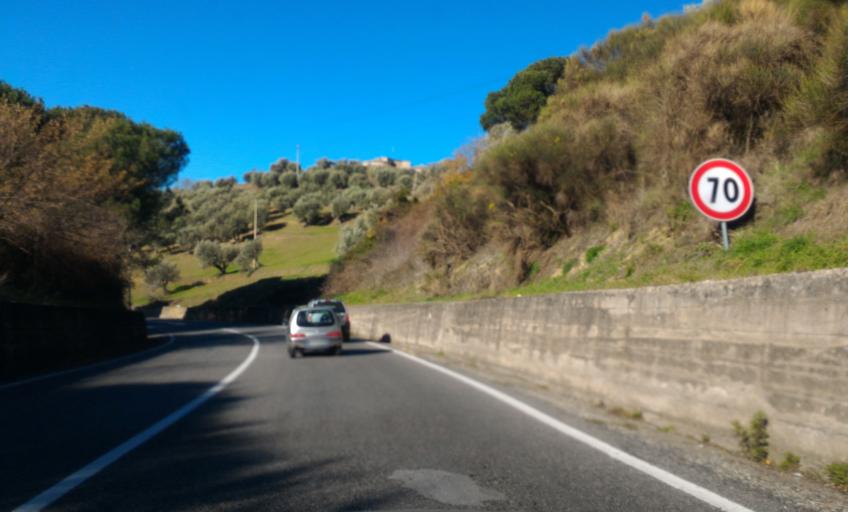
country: IT
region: Calabria
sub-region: Provincia di Cosenza
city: Cosenza
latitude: 39.2962
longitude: 16.2693
